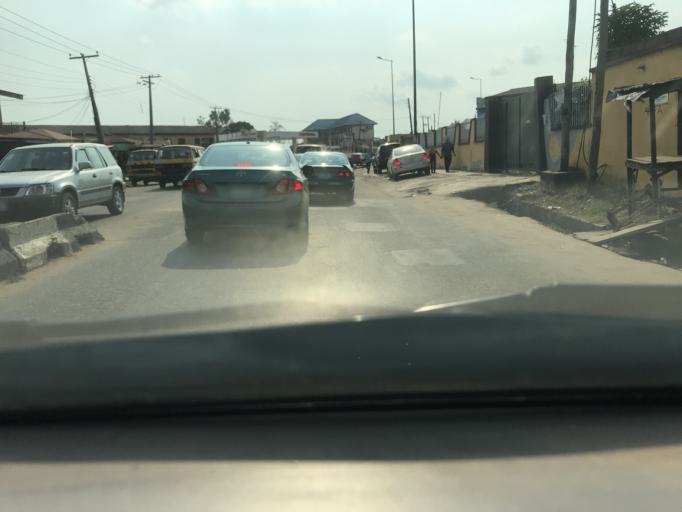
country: NG
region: Lagos
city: Agege
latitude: 6.5996
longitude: 3.2953
